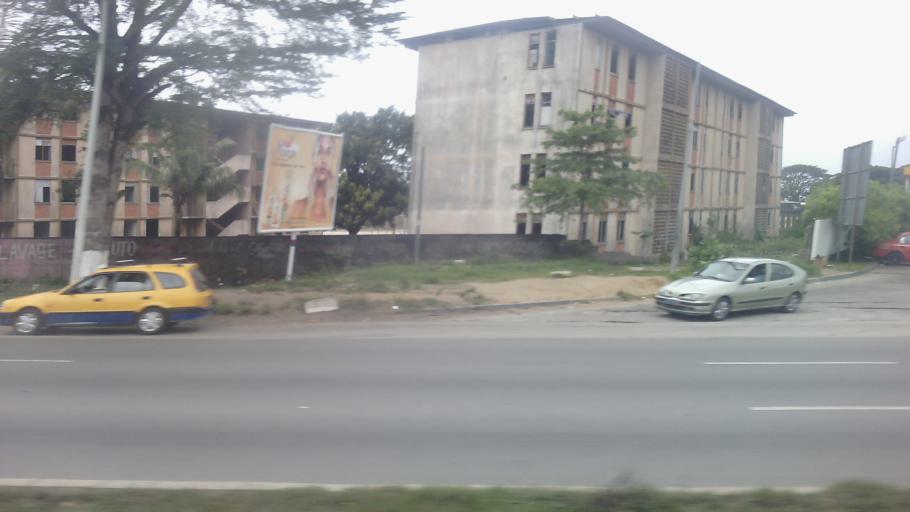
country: CI
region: Lagunes
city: Abidjan
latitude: 5.2631
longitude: -3.9600
